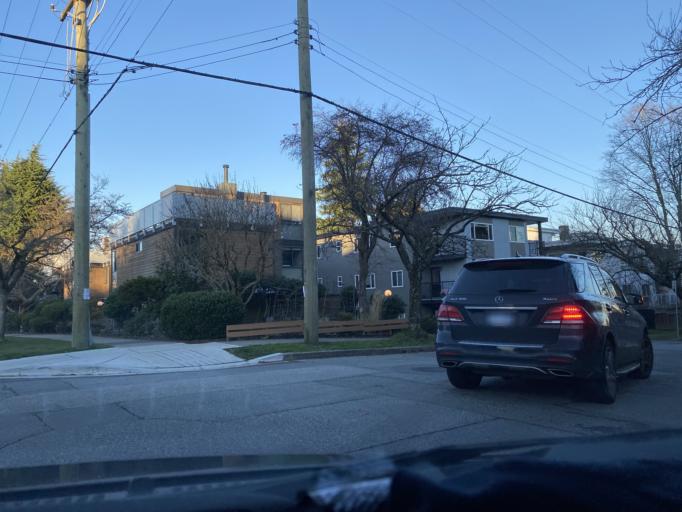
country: CA
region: British Columbia
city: West End
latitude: 49.2646
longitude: -123.1504
